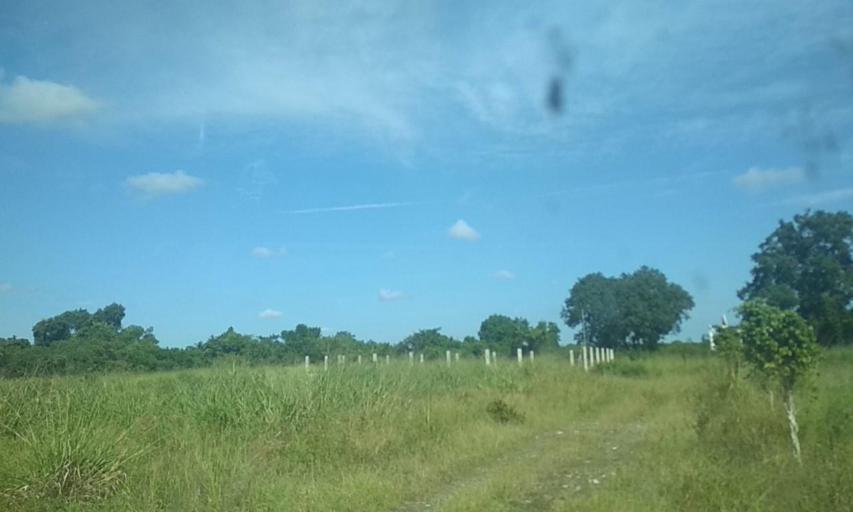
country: MX
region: Veracruz
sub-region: Martinez de la Torre
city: La Union Paso Largo
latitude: 20.1354
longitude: -96.9909
